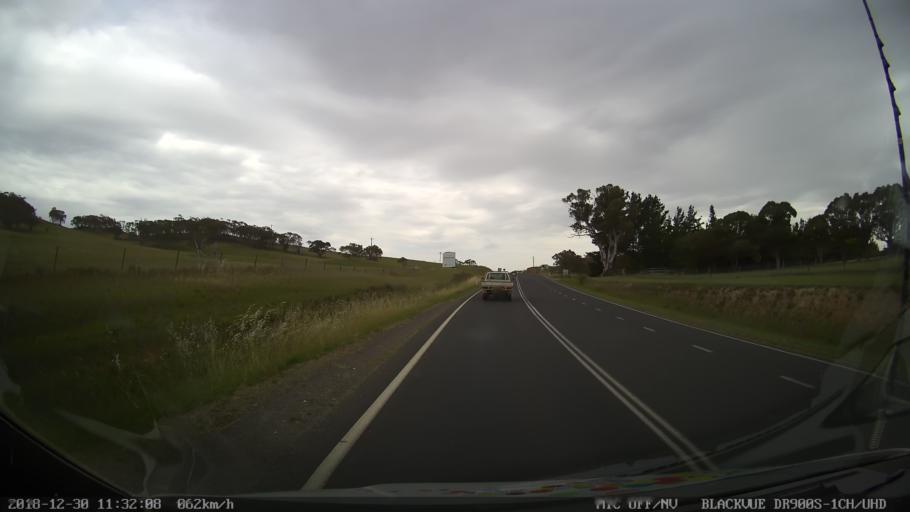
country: AU
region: New South Wales
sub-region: Snowy River
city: Jindabyne
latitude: -36.4244
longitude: 148.6092
